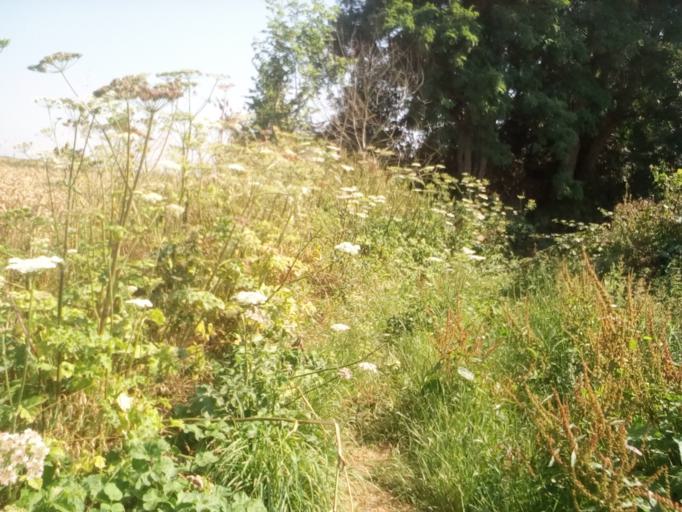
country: FR
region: Lower Normandy
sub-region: Departement du Calvados
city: Bernieres-sur-Mer
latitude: 49.3067
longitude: -0.4244
